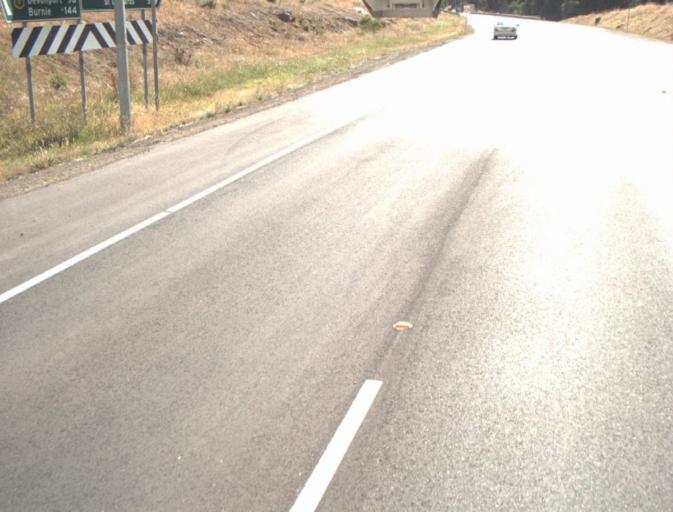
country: AU
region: Tasmania
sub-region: Launceston
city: Summerhill
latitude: -41.4837
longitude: 147.1515
